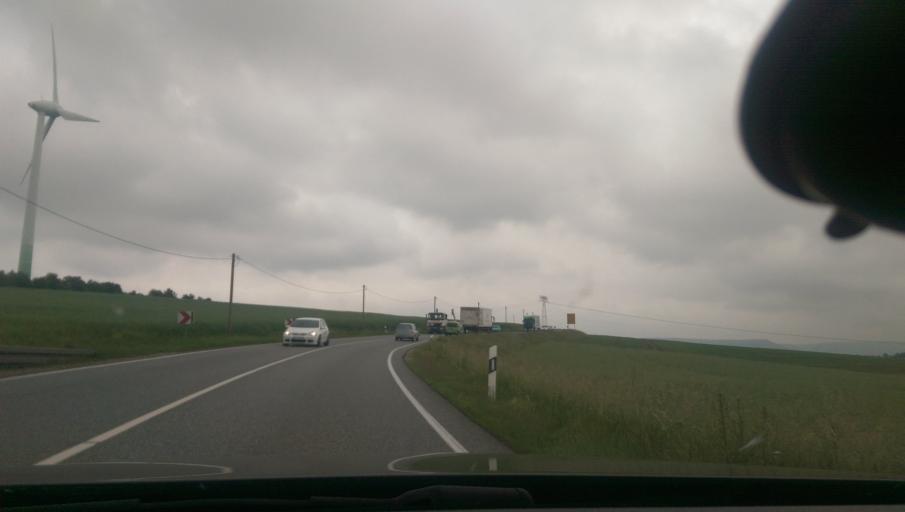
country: DE
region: Thuringia
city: Kleinfurra
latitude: 51.4406
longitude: 10.7904
